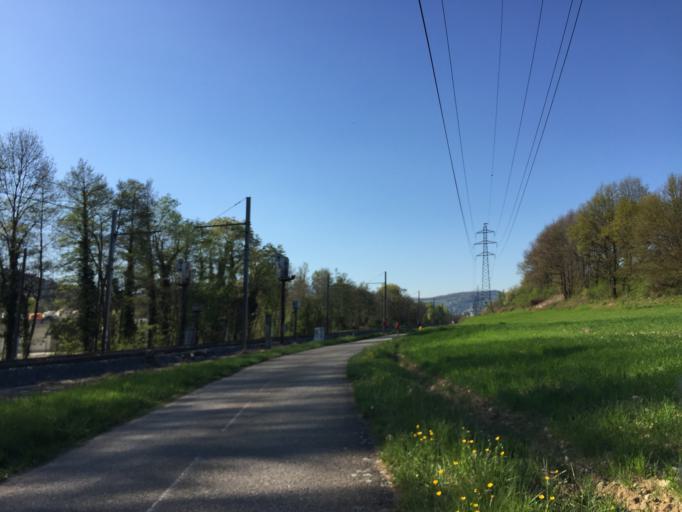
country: FR
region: Rhone-Alpes
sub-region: Departement de la Savoie
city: Saint-Baldoph
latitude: 45.5405
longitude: 5.9632
